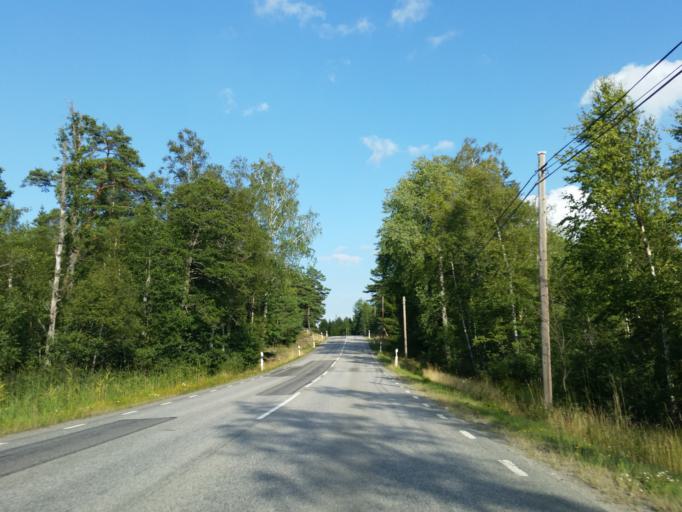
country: SE
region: Stockholm
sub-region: Nykvarns Kommun
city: Nykvarn
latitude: 59.2071
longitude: 17.3673
